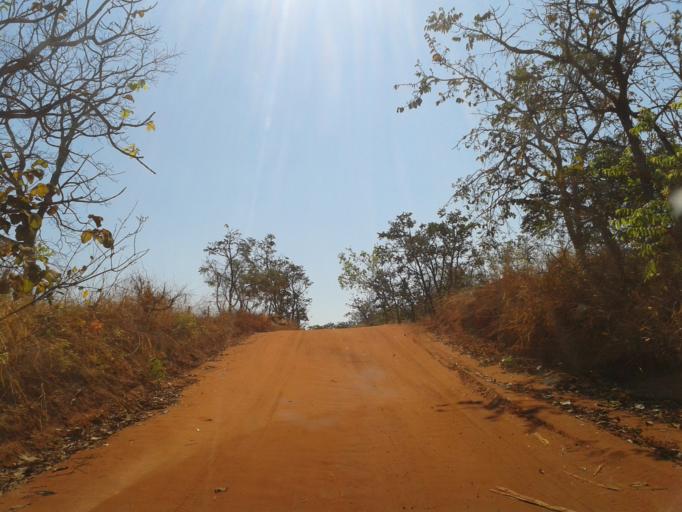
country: BR
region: Minas Gerais
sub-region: Ituiutaba
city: Ituiutaba
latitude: -19.0578
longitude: -49.3604
